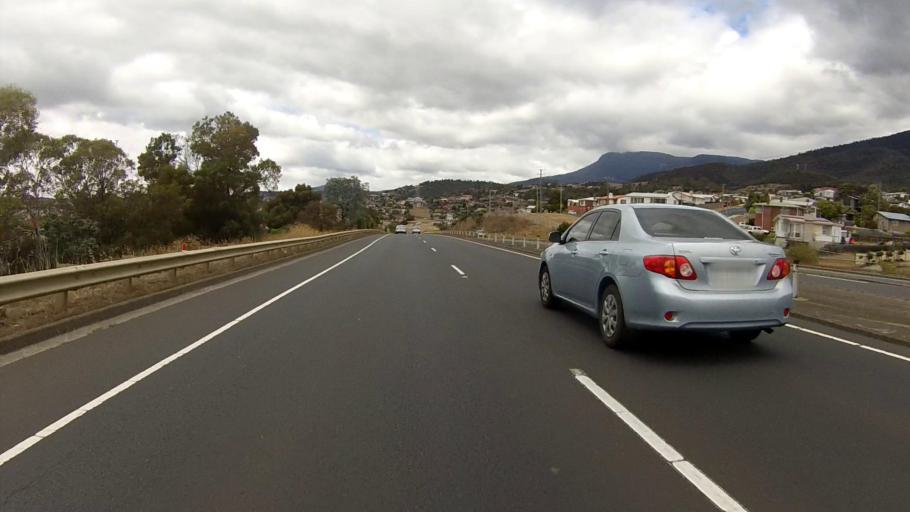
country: AU
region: Tasmania
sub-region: Glenorchy
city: Berriedale
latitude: -42.8077
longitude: 147.2496
